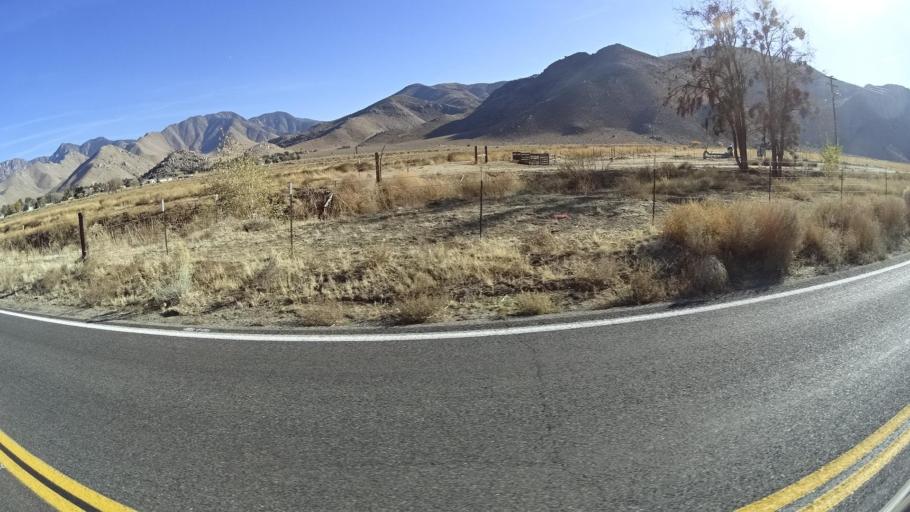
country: US
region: California
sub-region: Kern County
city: Weldon
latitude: 35.6902
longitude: -118.2323
